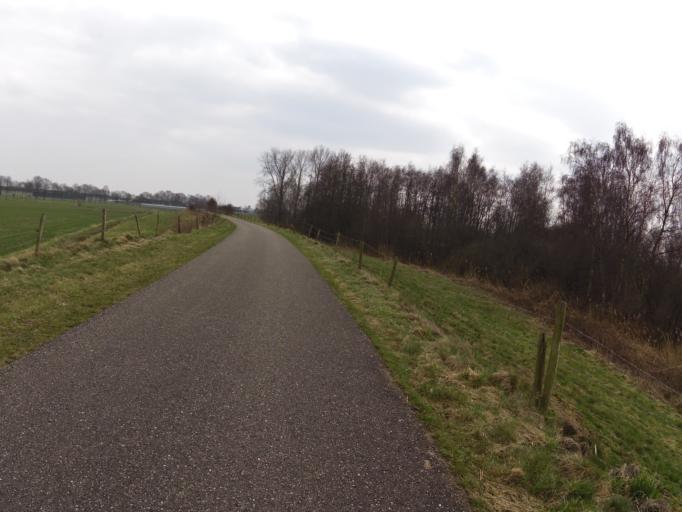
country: NL
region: North Brabant
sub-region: Gemeente Heusden
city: Heusden
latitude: 51.7030
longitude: 5.1146
